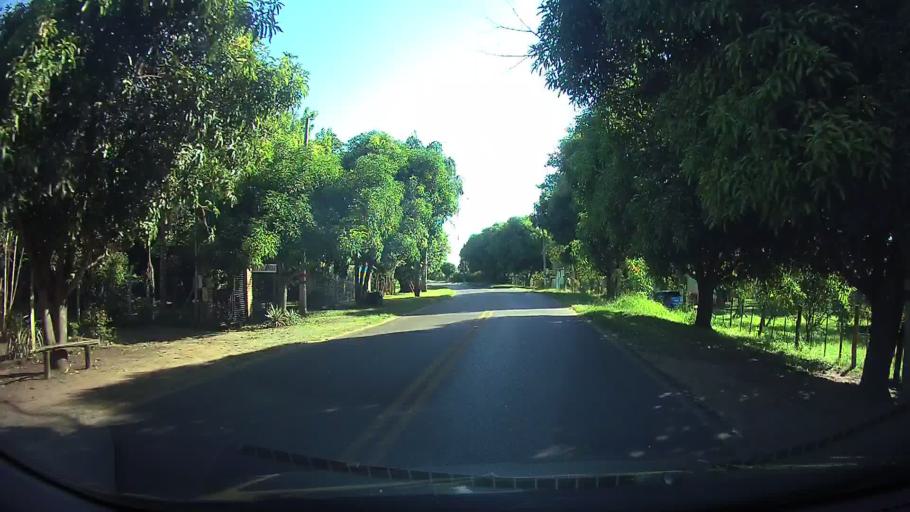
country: PY
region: Cordillera
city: Atyra
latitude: -25.2943
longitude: -57.1840
